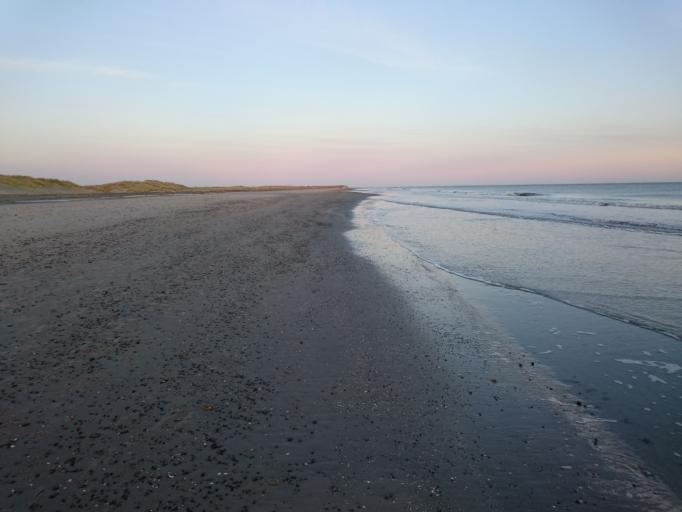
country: DK
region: North Denmark
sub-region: Frederikshavn Kommune
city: Skagen
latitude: 57.7408
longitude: 10.6404
